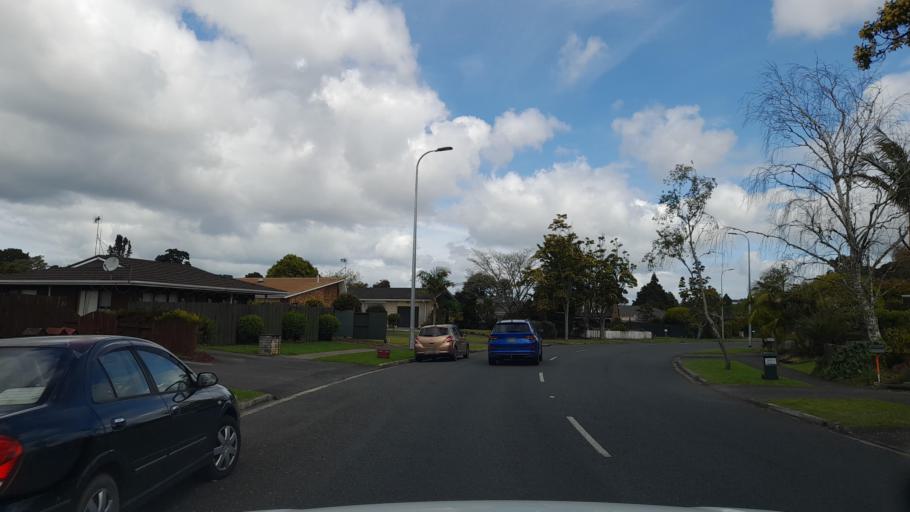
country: NZ
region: Northland
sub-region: Whangarei
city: Whangarei
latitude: -35.6882
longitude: 174.3006
